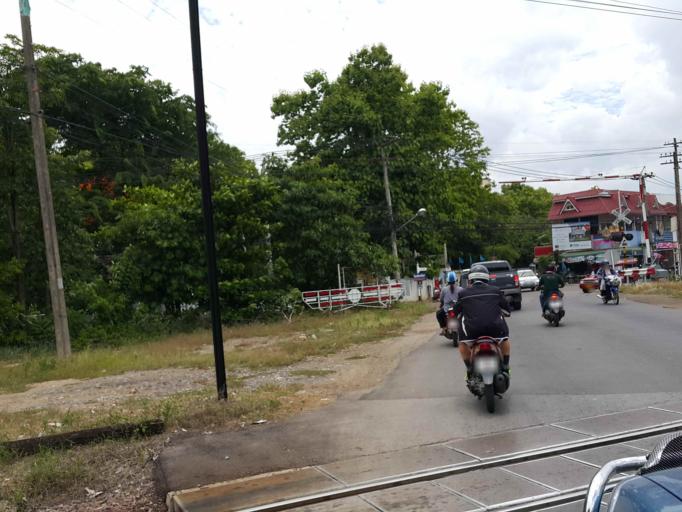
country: TH
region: Chiang Mai
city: Chiang Mai
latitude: 18.7778
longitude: 99.0172
